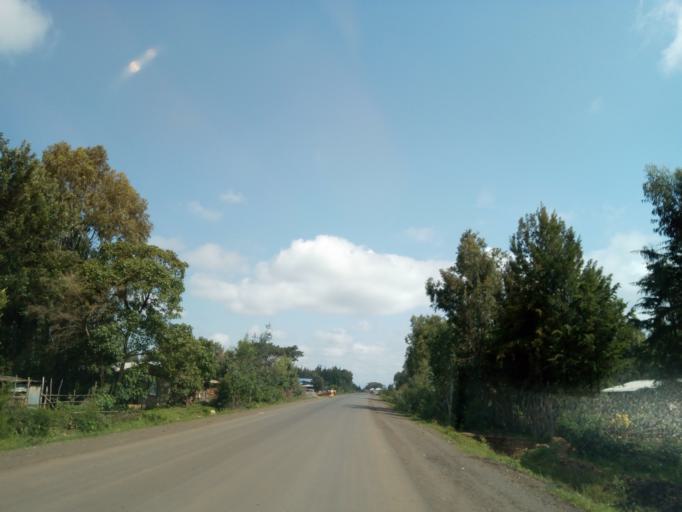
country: ET
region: Oromiya
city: Waliso
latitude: 8.5464
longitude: 37.9605
